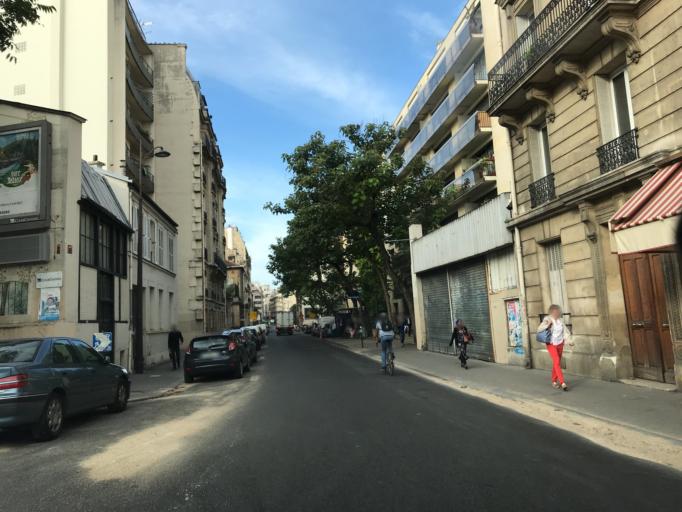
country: FR
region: Ile-de-France
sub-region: Departement des Hauts-de-Seine
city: Malakoff
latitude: 48.8420
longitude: 2.3129
